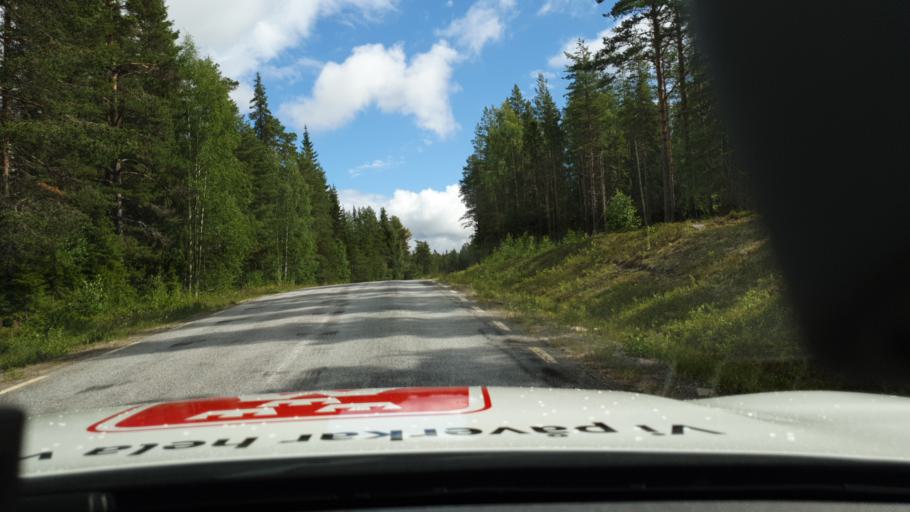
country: SE
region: Norrbotten
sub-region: Pitea Kommun
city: Rosvik
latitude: 65.4163
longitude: 21.7780
